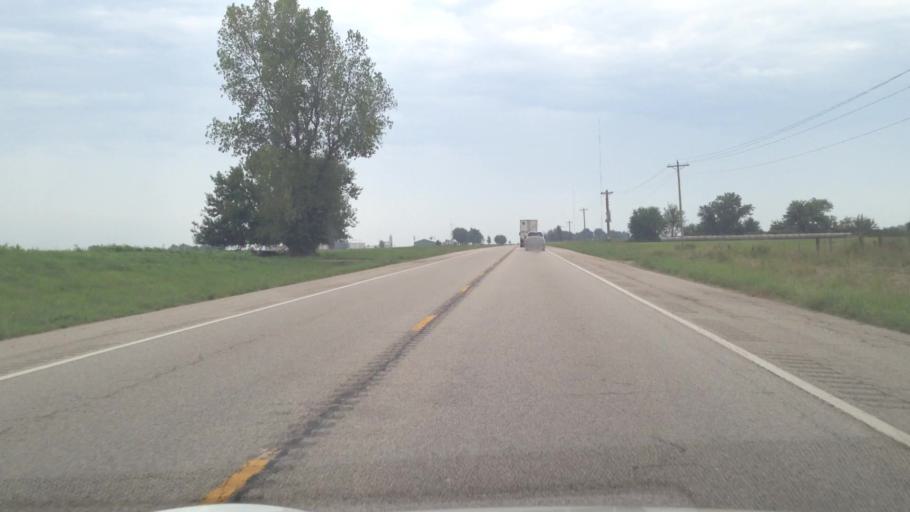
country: US
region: Missouri
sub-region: Jasper County
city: Carl Junction
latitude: 37.2447
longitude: -94.7051
